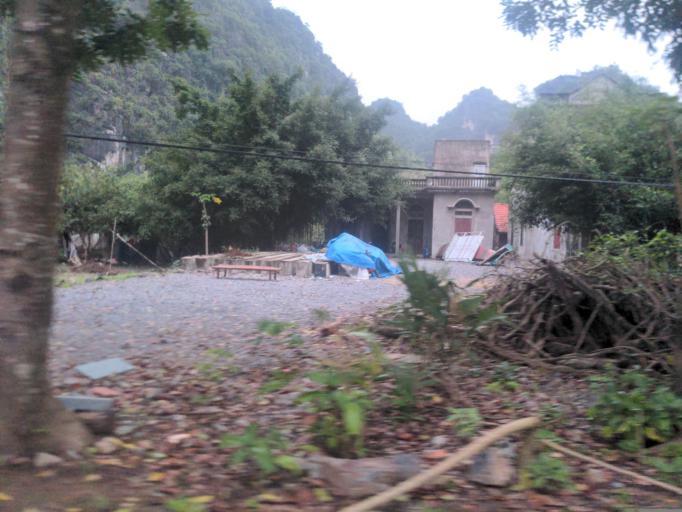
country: VN
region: Ninh Binh
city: Thi Tran Tam Diep
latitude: 20.2146
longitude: 105.9161
